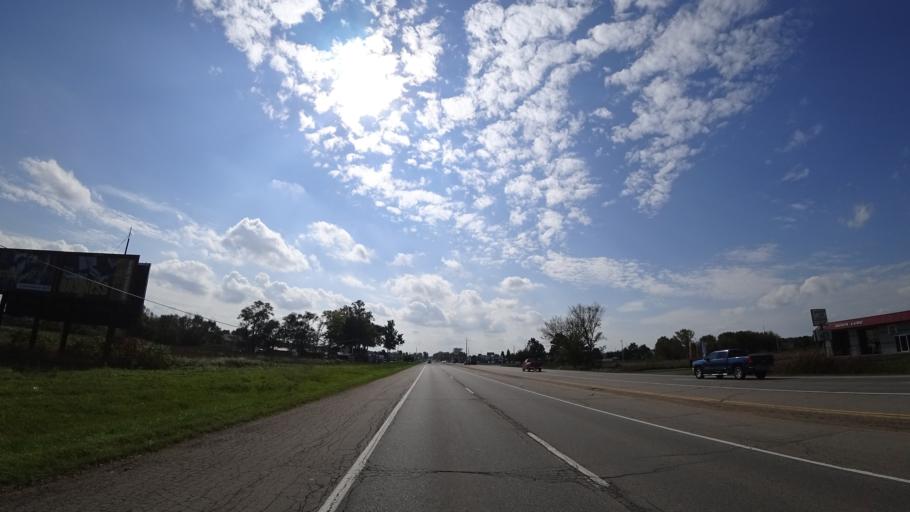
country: US
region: Michigan
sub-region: Saint Joseph County
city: Three Rivers
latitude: 41.9373
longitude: -85.6515
